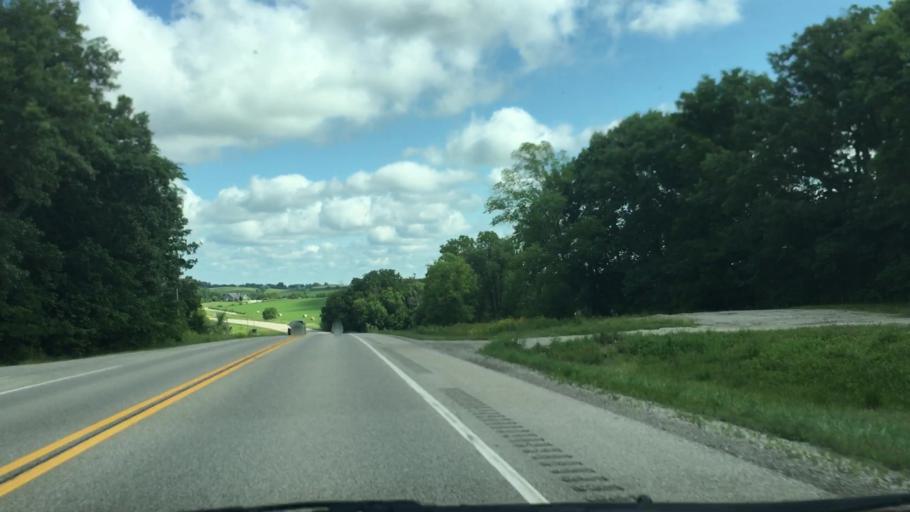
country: US
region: Iowa
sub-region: Johnson County
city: Solon
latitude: 41.7467
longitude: -91.4738
